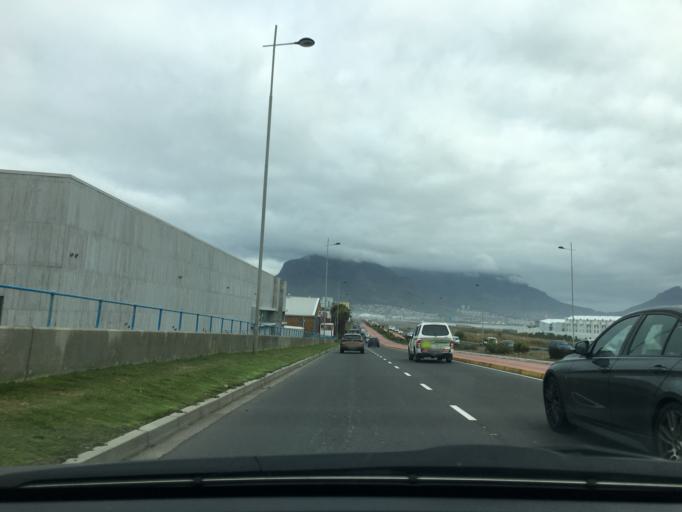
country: ZA
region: Western Cape
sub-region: City of Cape Town
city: Sunset Beach
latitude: -33.8936
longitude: 18.4840
